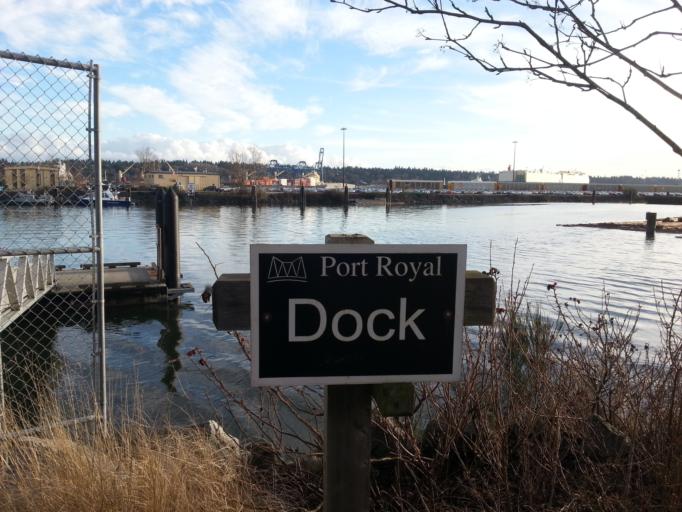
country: CA
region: British Columbia
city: New Westminster
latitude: 49.1938
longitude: -122.9223
